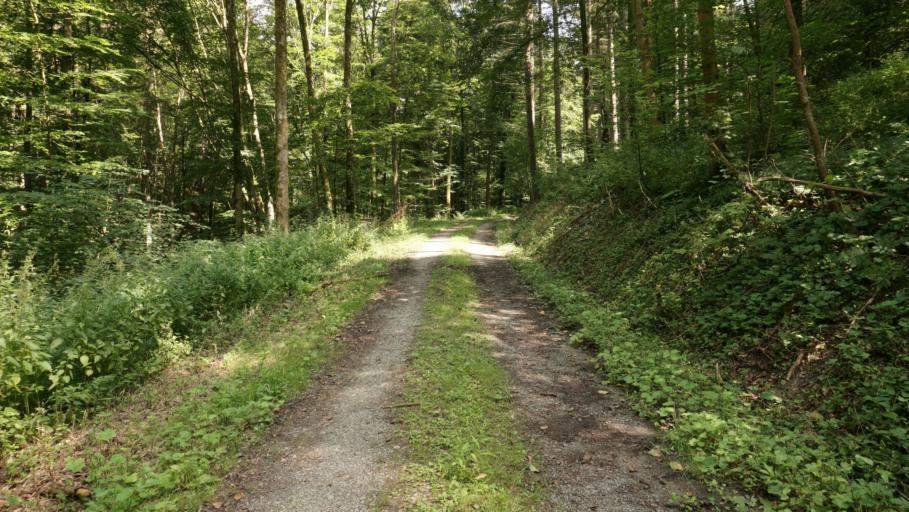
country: DE
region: Baden-Wuerttemberg
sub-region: Karlsruhe Region
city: Mosbach
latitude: 49.3360
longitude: 9.1547
